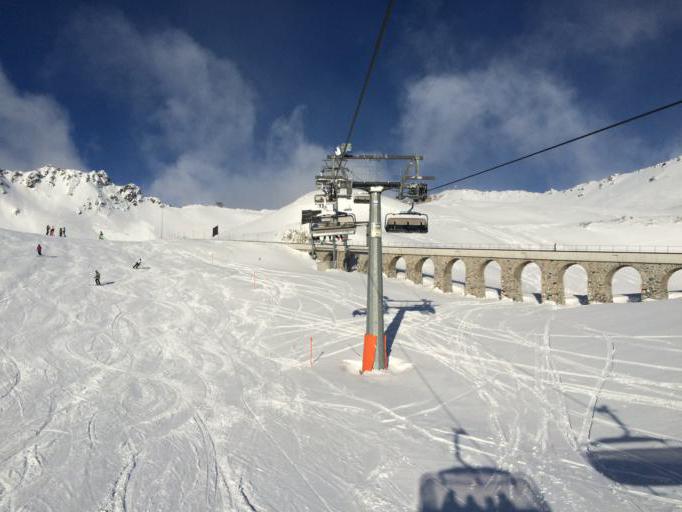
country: CH
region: Grisons
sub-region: Praettigau/Davos District
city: Davos
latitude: 46.8263
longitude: 9.8131
